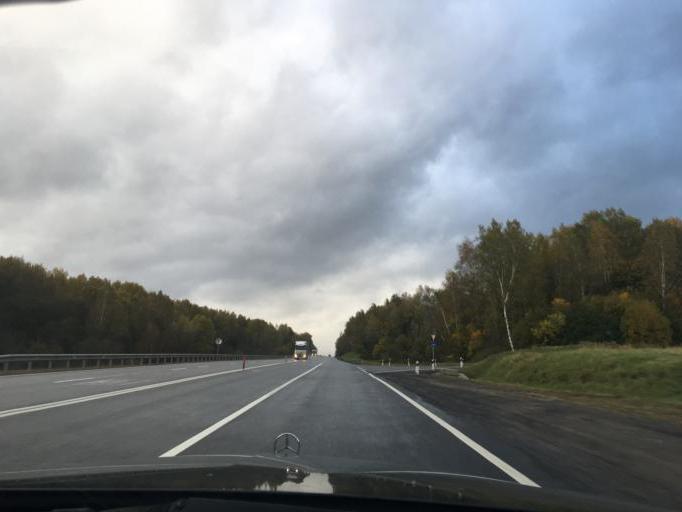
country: RU
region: Smolensk
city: Pechersk
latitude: 54.8986
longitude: 32.1189
